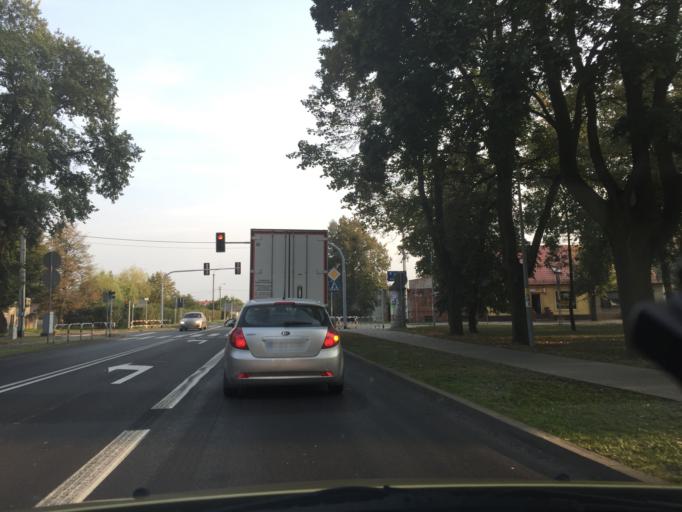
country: PL
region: Greater Poland Voivodeship
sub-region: Powiat jarocinski
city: Jarocin
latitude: 52.0239
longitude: 17.4642
